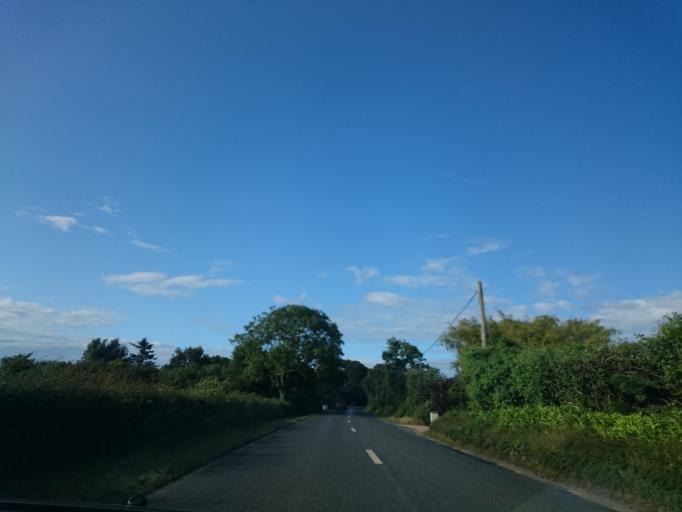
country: IE
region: Leinster
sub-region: Loch Garman
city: Loch Garman
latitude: 52.2798
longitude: -6.4675
